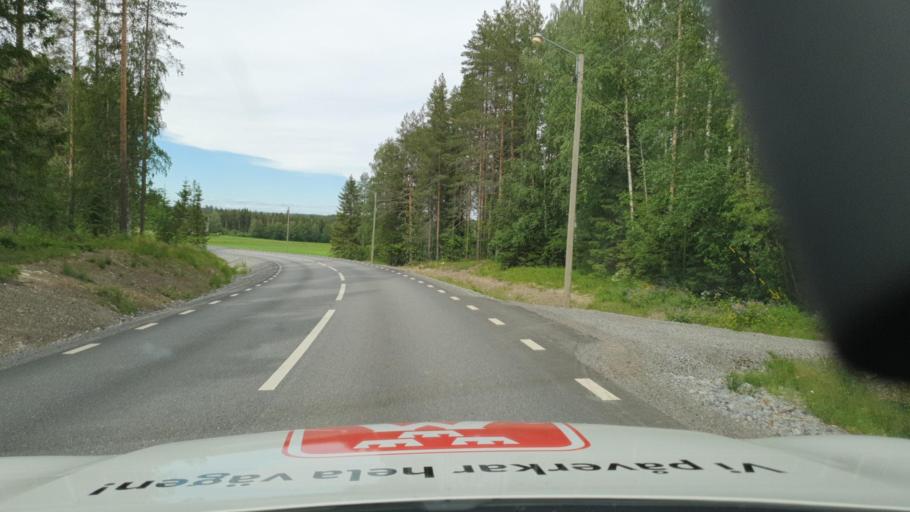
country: SE
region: Vaesterbotten
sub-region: Skelleftea Kommun
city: Burtraesk
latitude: 64.4967
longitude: 20.6280
